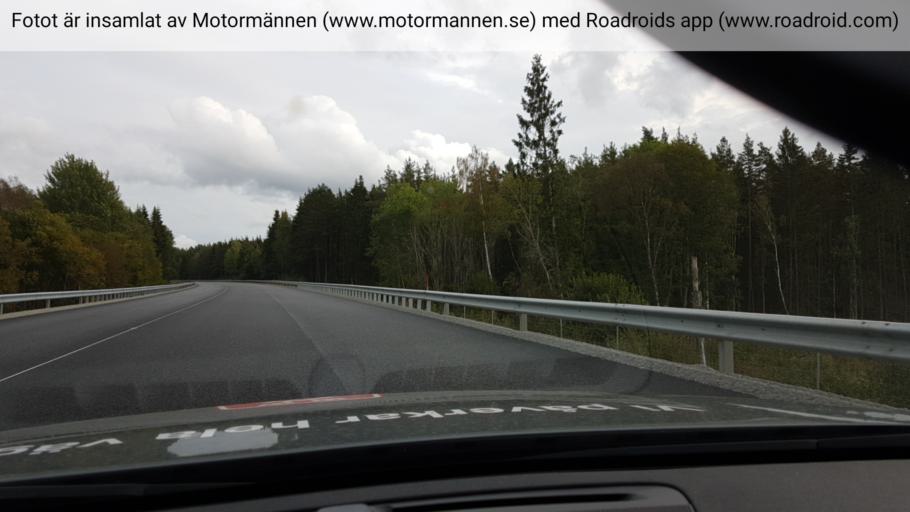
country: SE
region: Stockholm
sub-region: Norrtalje Kommun
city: Norrtalje
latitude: 59.7384
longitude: 18.7276
